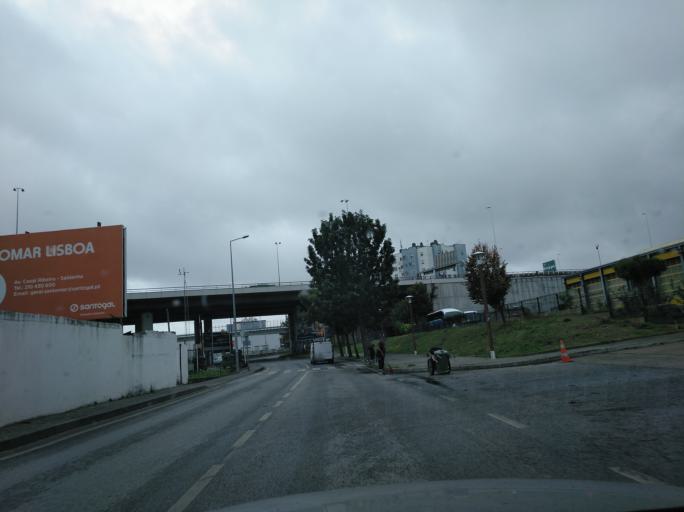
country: PT
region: Lisbon
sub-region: Loures
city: Sacavem
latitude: 38.7893
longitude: -9.1037
